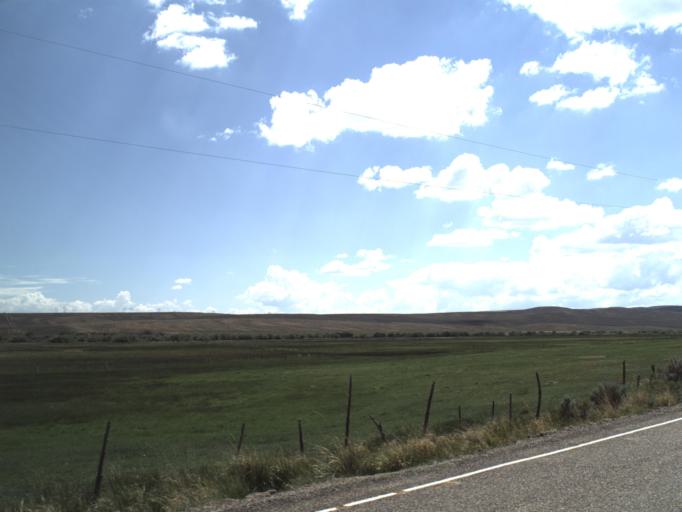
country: US
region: Utah
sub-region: Rich County
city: Randolph
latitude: 41.5241
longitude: -111.1840
